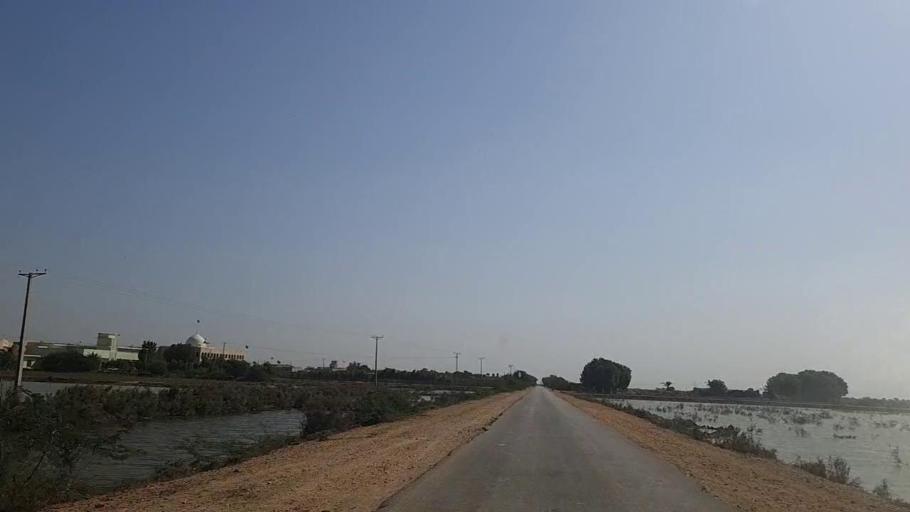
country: PK
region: Sindh
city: Mirpur Batoro
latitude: 24.6427
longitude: 68.2903
